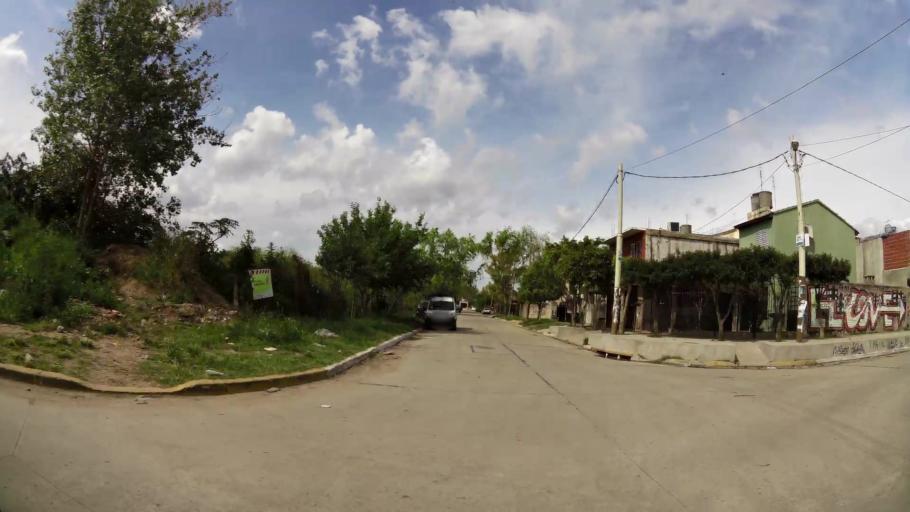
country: AR
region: Buenos Aires
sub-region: Partido de Quilmes
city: Quilmes
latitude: -34.7588
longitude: -58.2516
